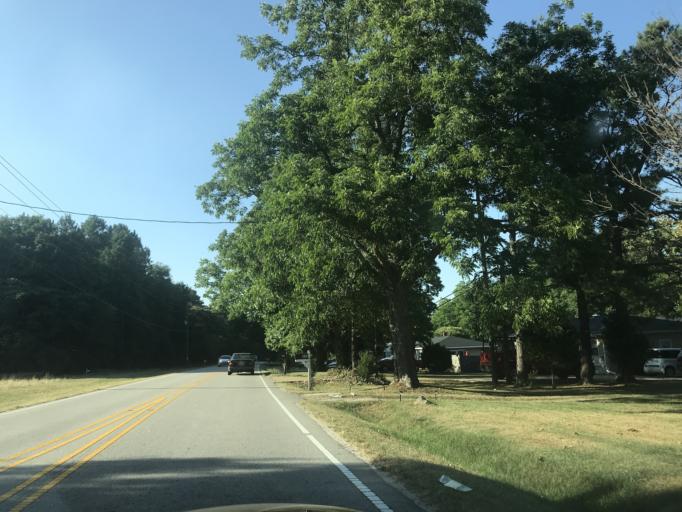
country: US
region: North Carolina
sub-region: Wake County
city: Garner
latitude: 35.7166
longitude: -78.6024
